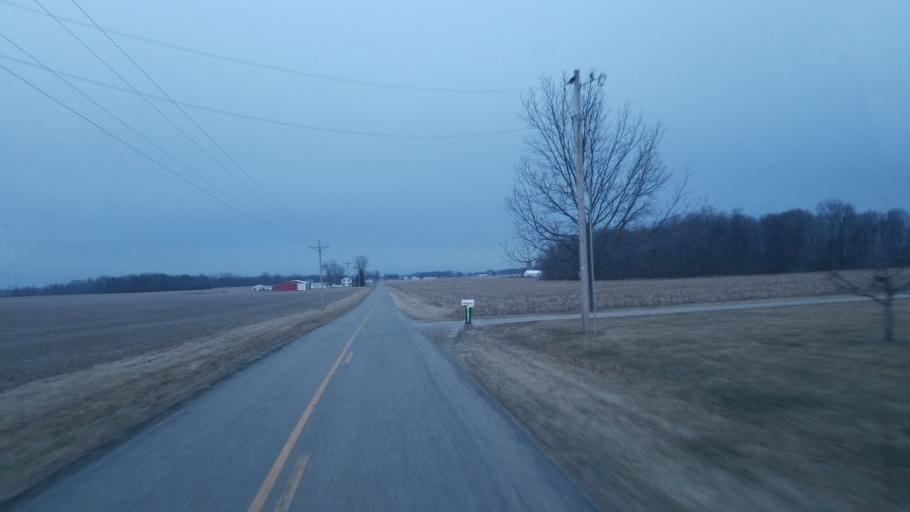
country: US
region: Ohio
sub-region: Defiance County
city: Hicksville
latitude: 41.3343
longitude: -84.7285
